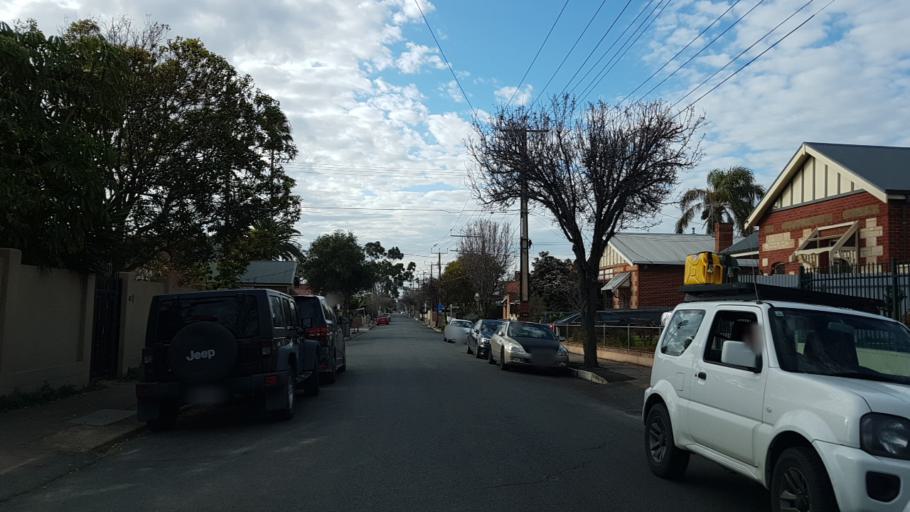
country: AU
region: South Australia
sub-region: Prospect
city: Prospect
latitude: -34.8900
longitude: 138.5896
